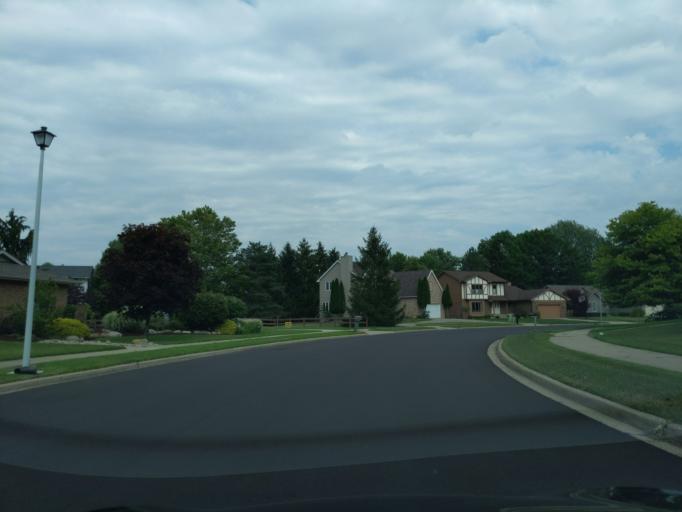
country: US
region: Michigan
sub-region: Ingham County
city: Okemos
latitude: 42.7384
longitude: -84.4353
